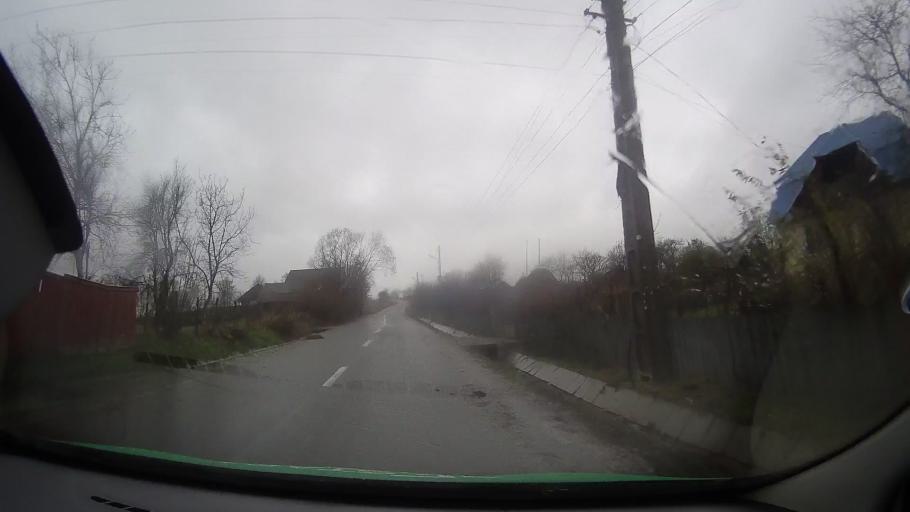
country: RO
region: Mures
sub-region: Comuna Vatava
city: Vatava
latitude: 46.9587
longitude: 24.7574
